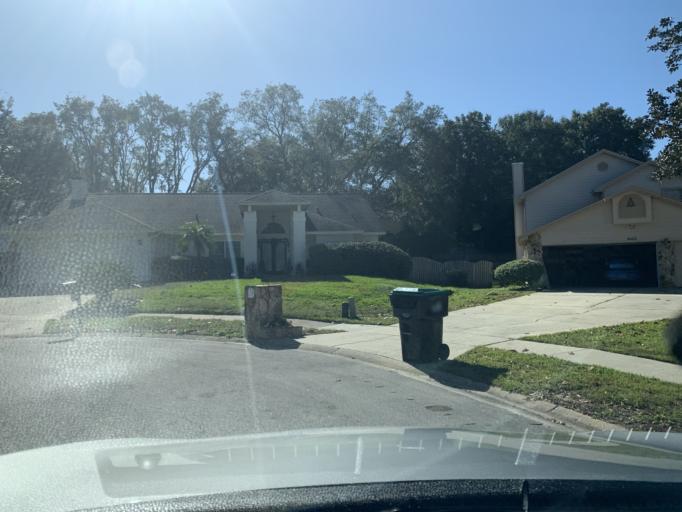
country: US
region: Florida
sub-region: Orange County
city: Clarcona
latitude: 28.6299
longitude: -81.4758
